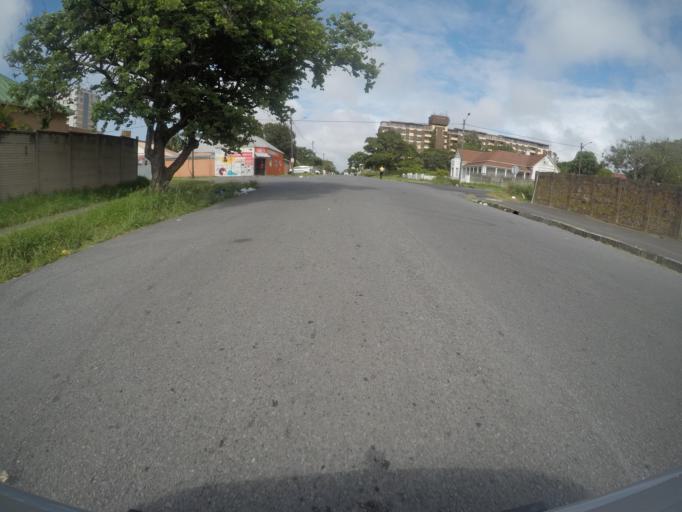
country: ZA
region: Eastern Cape
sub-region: Buffalo City Metropolitan Municipality
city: East London
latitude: -32.9988
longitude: 27.9075
